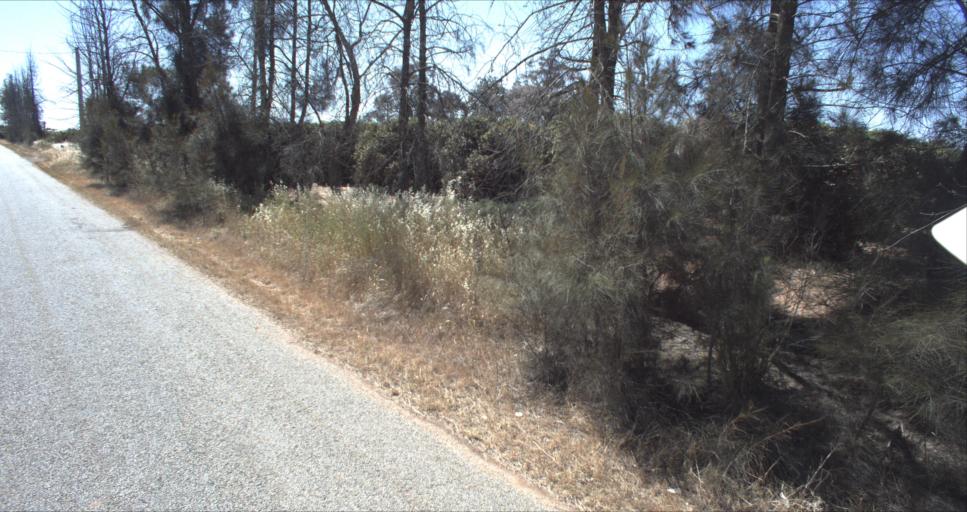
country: AU
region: New South Wales
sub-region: Leeton
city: Leeton
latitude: -34.5357
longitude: 146.3574
